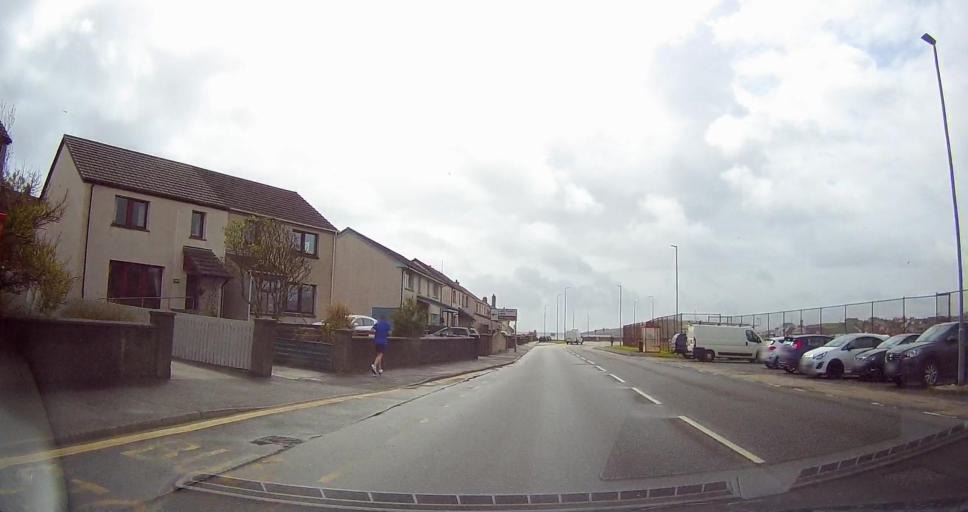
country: GB
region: Scotland
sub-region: Shetland Islands
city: Lerwick
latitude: 60.1513
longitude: -1.1602
